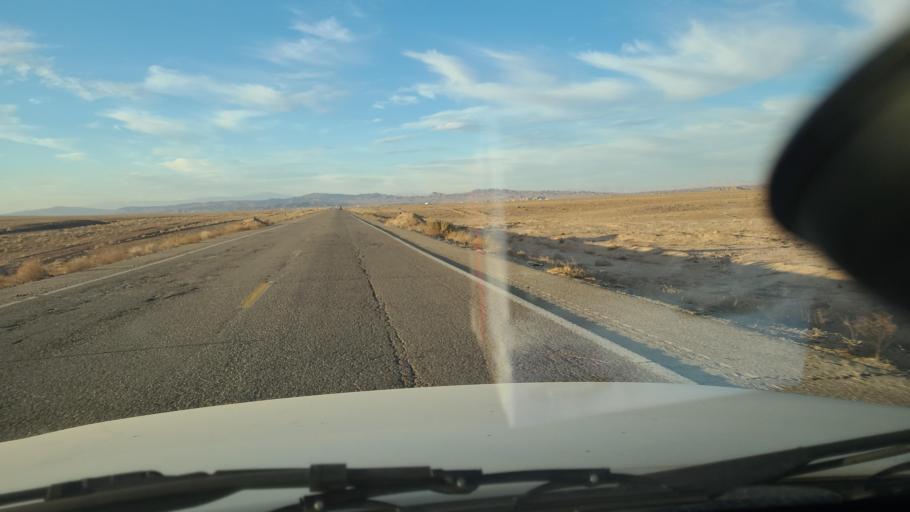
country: IR
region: Razavi Khorasan
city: Neqab
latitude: 36.8327
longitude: 57.5560
